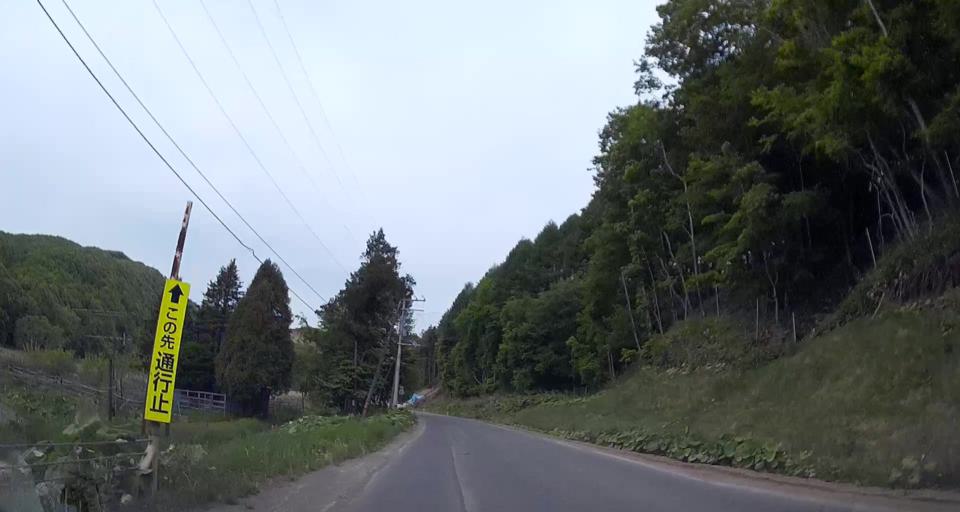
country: JP
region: Hokkaido
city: Chitose
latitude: 42.7583
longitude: 141.9792
